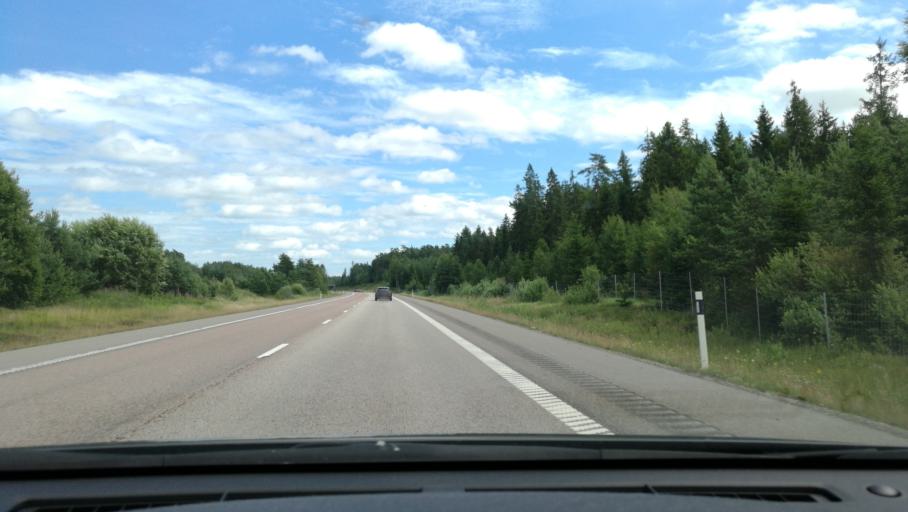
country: SE
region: Uppsala
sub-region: Enkopings Kommun
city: Grillby
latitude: 59.6421
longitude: 17.2090
